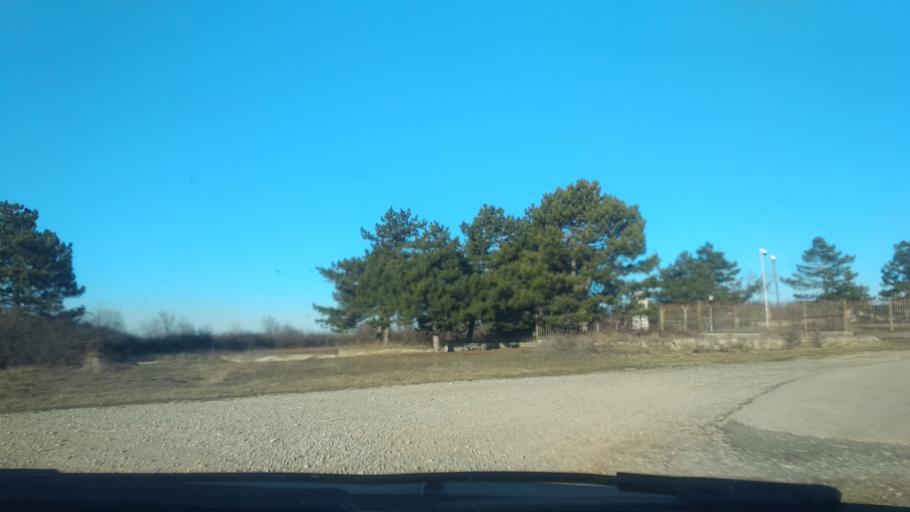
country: XK
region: Pristina
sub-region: Kosovo Polje
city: Kosovo Polje
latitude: 42.6902
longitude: 21.1222
